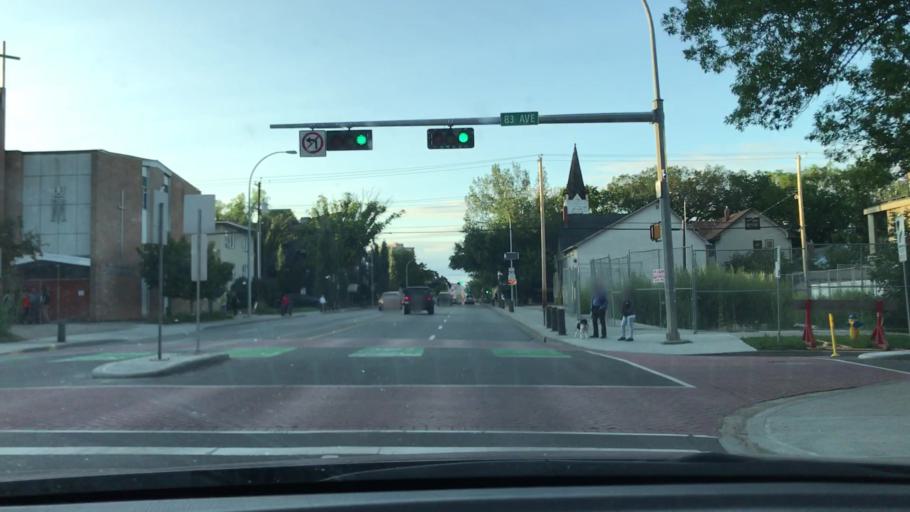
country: CA
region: Alberta
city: Edmonton
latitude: 53.5189
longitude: -113.4862
